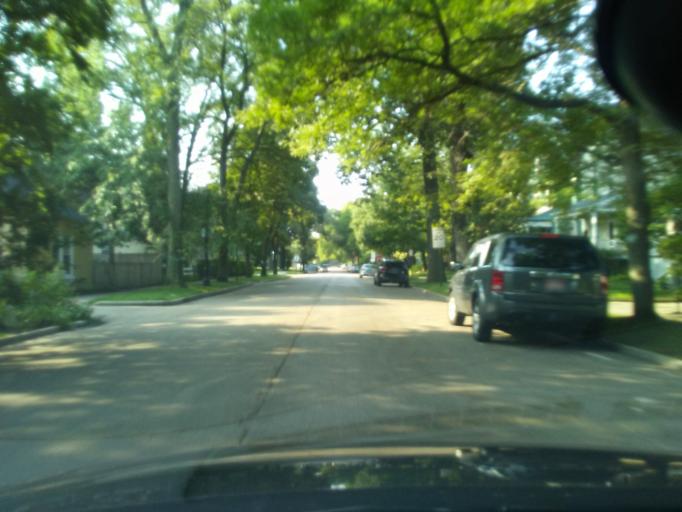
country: US
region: Illinois
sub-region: Cook County
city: Evanston
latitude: 42.0384
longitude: -87.6837
